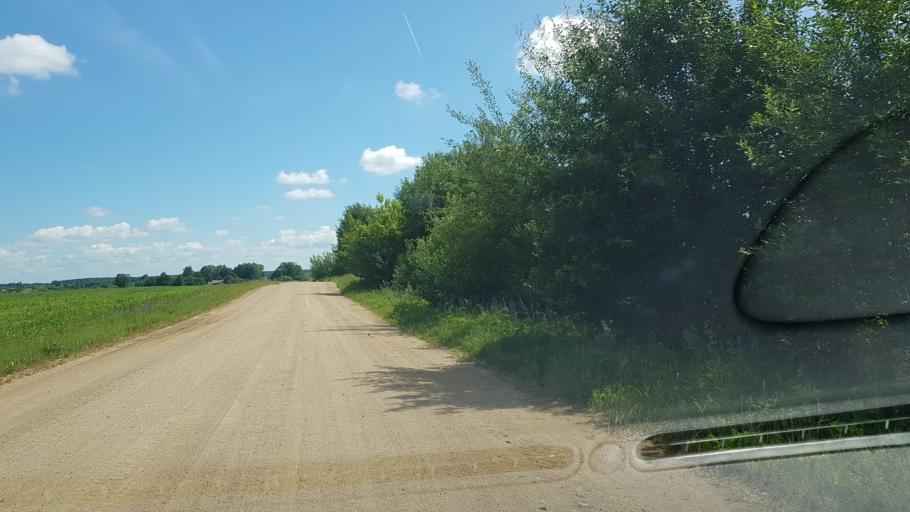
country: BY
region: Vitebsk
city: Dubrowna
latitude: 54.4795
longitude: 30.7740
